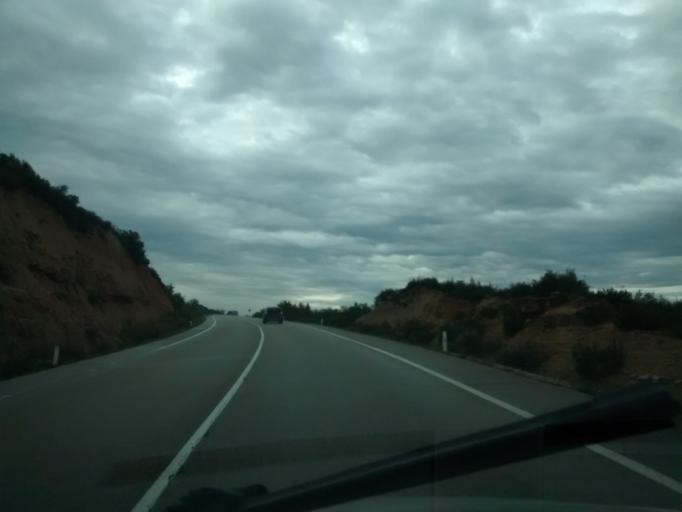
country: ES
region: Aragon
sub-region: Provincia de Zaragoza
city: Maella
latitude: 41.1419
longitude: 0.1183
